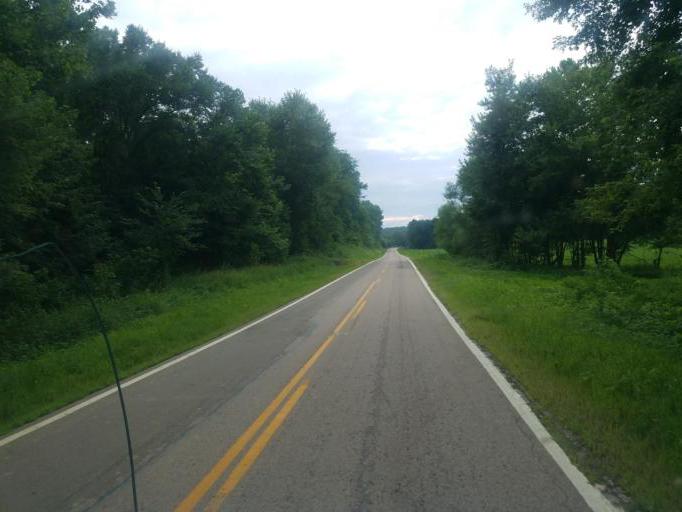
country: US
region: Ohio
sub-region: Knox County
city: Oak Hill
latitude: 40.3546
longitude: -82.0979
